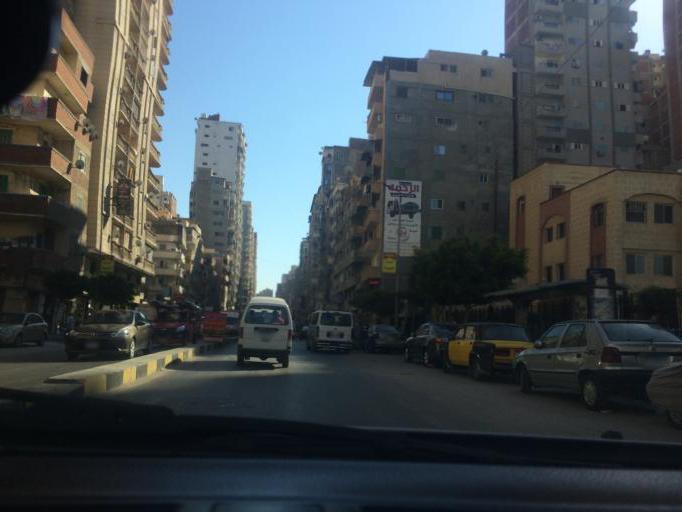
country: EG
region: Alexandria
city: Alexandria
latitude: 31.2614
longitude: 29.9922
